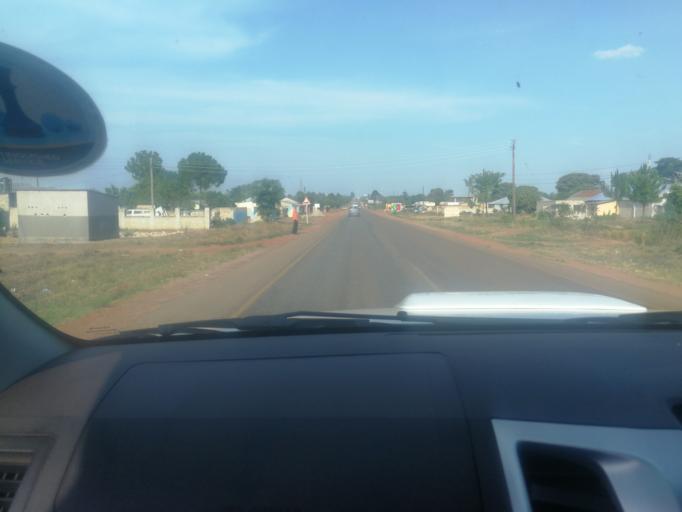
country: ZM
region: Northern
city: Kasama
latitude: -10.2151
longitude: 31.1512
